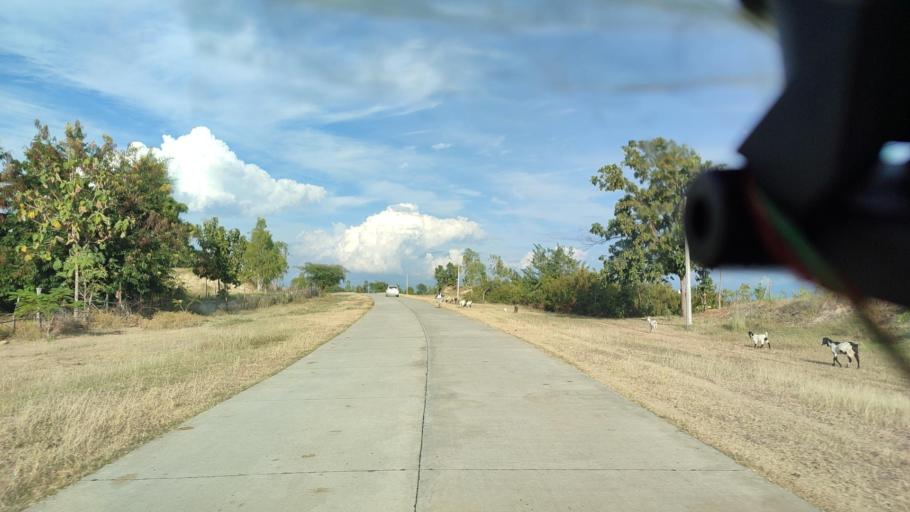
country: MM
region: Mandalay
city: Yamethin
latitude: 20.1086
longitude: 96.0542
